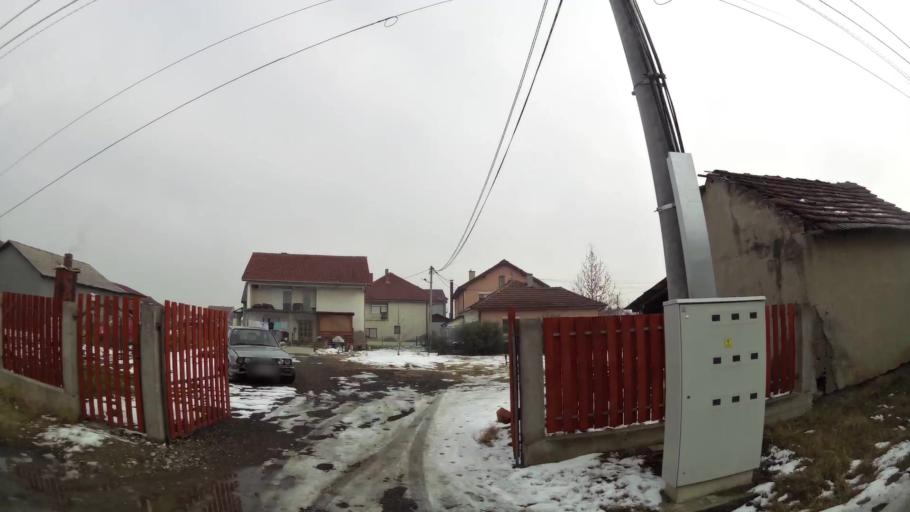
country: MK
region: Ilinden
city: Ilinden
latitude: 41.9923
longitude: 21.5731
